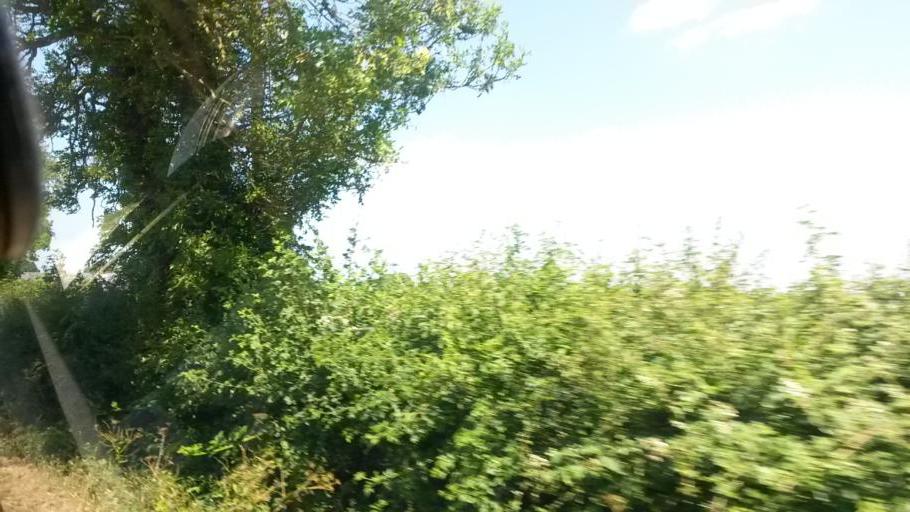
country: IE
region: Leinster
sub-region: Fingal County
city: Swords
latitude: 53.5318
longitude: -6.2508
